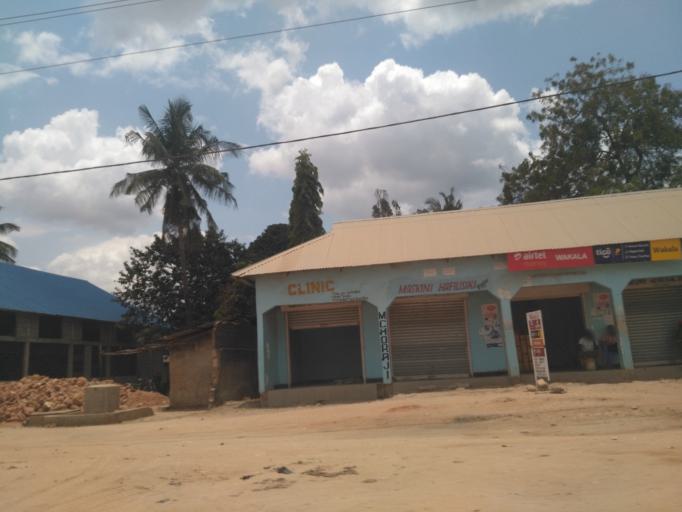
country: TZ
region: Dar es Salaam
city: Dar es Salaam
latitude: -6.8416
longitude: 39.3207
